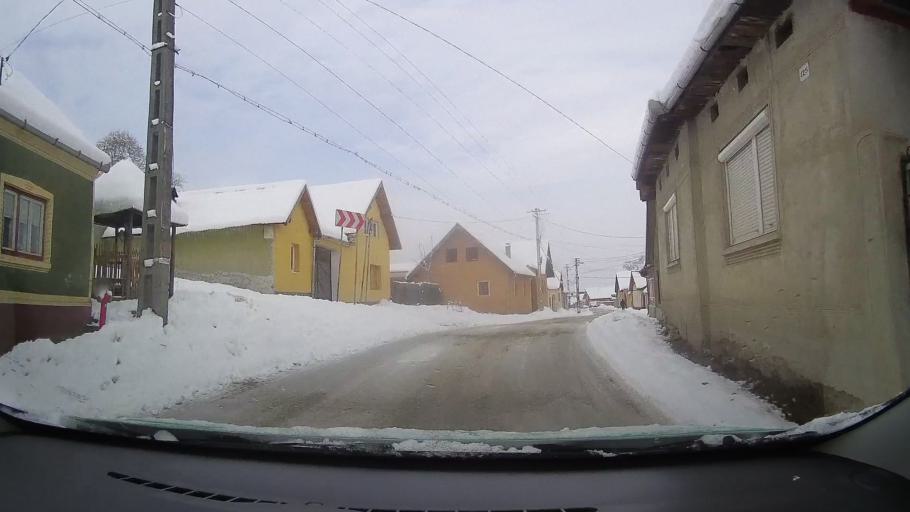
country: RO
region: Alba
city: Pianu de Sus
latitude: 45.8909
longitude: 23.4849
